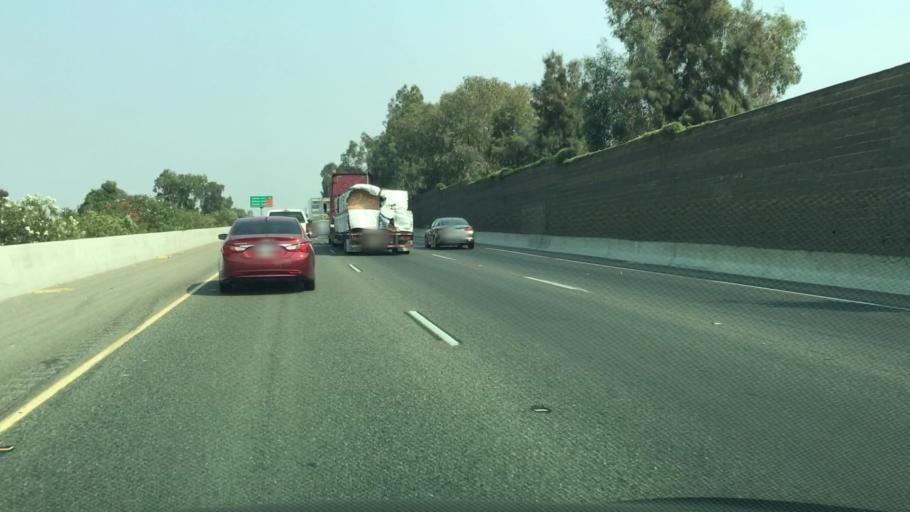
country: US
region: California
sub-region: Fresno County
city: West Park
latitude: 36.8027
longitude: -119.8790
